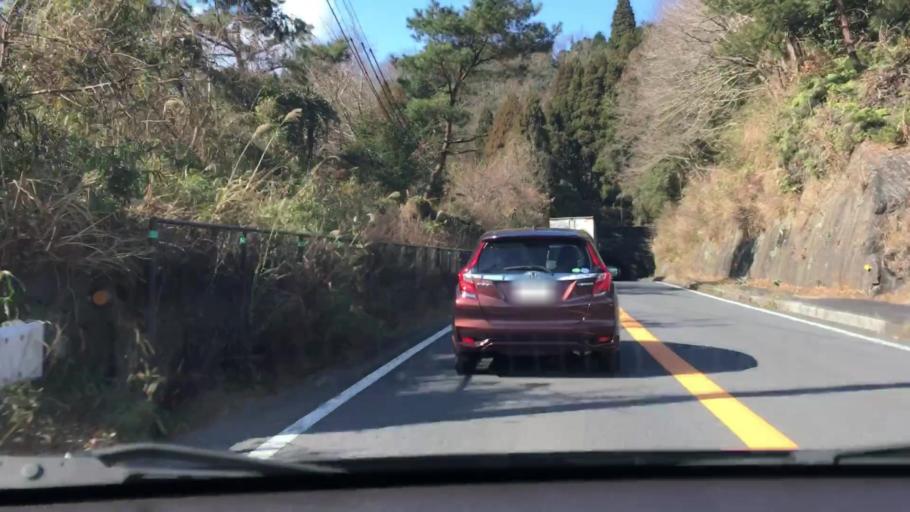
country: JP
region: Oita
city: Saiki
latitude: 32.9907
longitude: 131.8311
